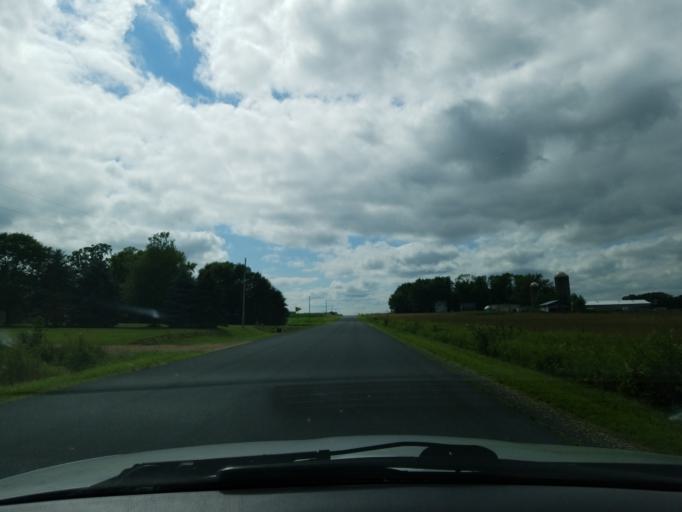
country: US
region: Wisconsin
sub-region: Saint Croix County
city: Woodville
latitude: 45.0036
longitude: -92.2816
